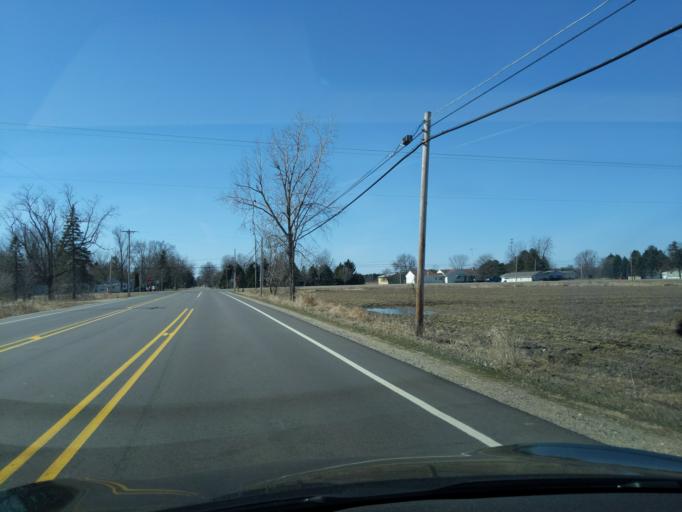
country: US
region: Michigan
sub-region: Eaton County
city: Grand Ledge
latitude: 42.7264
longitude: -84.7379
